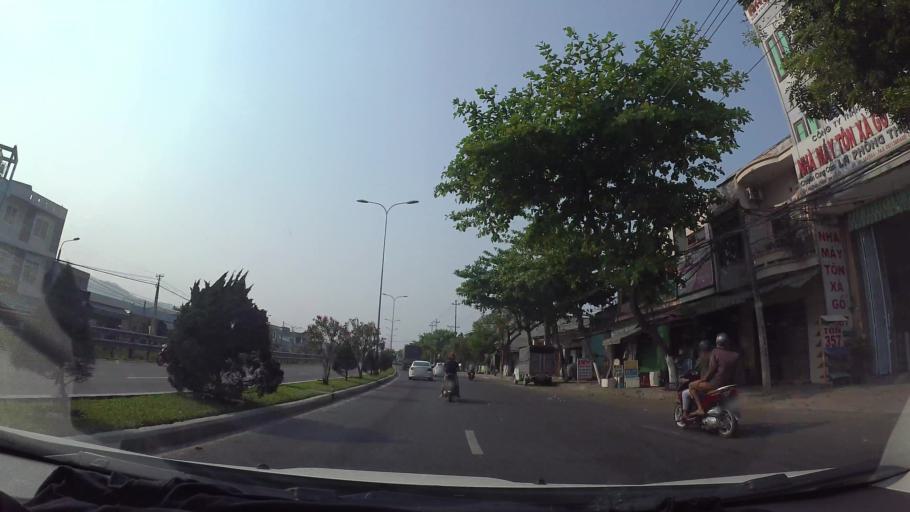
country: VN
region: Da Nang
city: Cam Le
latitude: 16.0218
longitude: 108.1935
